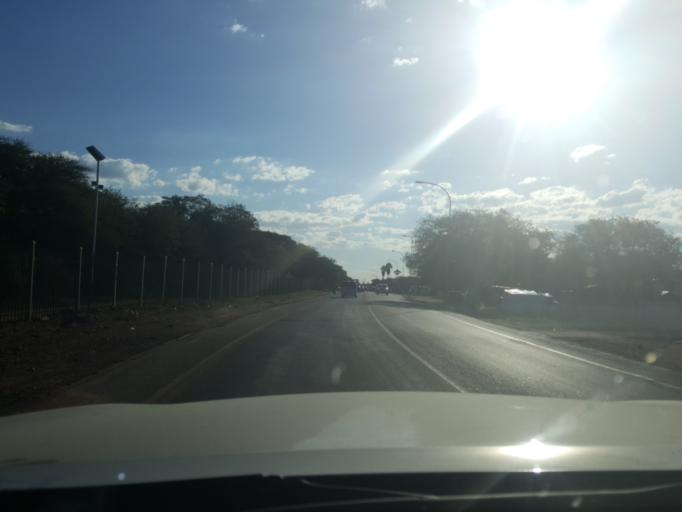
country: BW
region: South East
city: Gaborone
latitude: -24.6448
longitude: 25.9347
